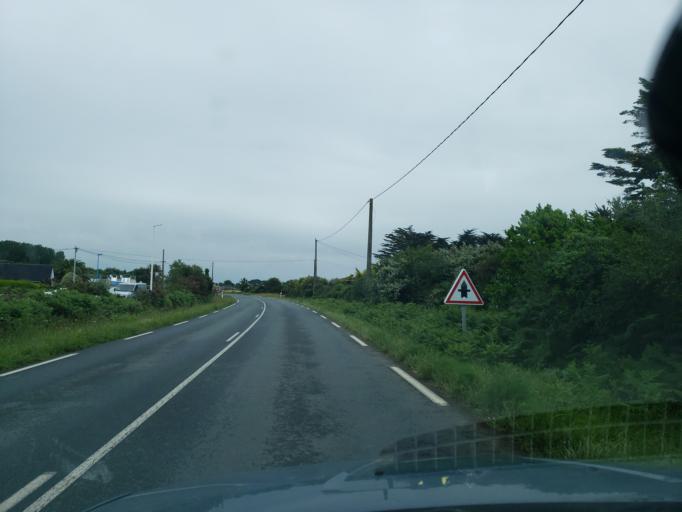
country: FR
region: Brittany
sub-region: Departement du Finistere
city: Plomeur
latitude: 47.8182
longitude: -4.3106
